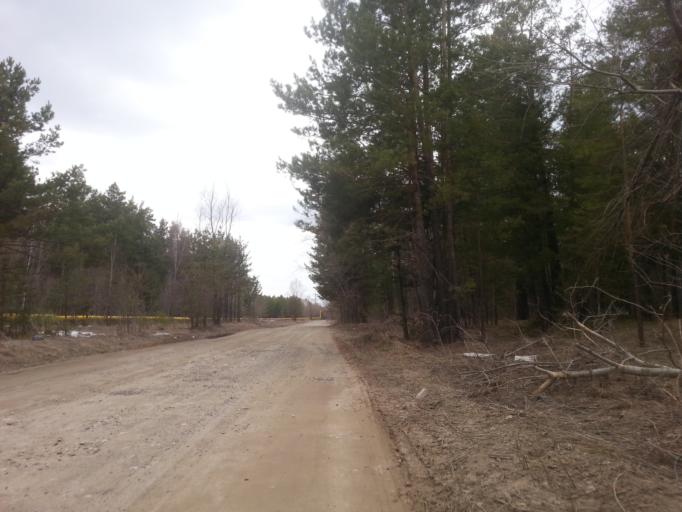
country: RU
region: Altai Krai
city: Yuzhnyy
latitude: 53.2828
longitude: 83.7331
